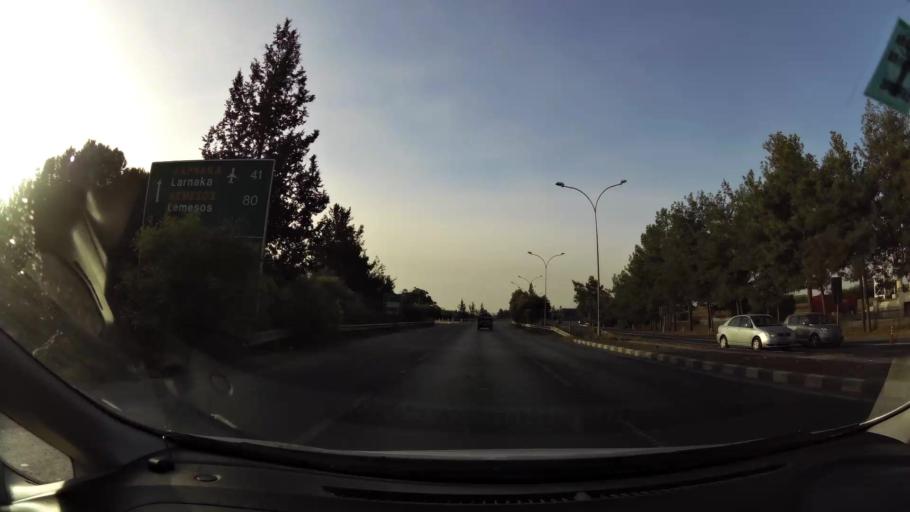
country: CY
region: Lefkosia
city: Nicosia
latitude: 35.1388
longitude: 33.3750
